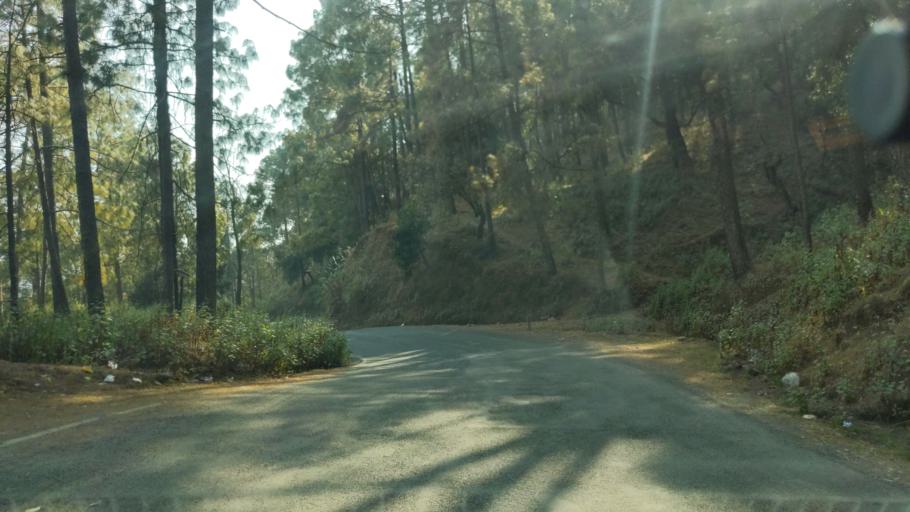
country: IN
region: Uttarakhand
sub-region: Naini Tal
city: Bhowali
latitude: 29.3940
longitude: 79.5392
